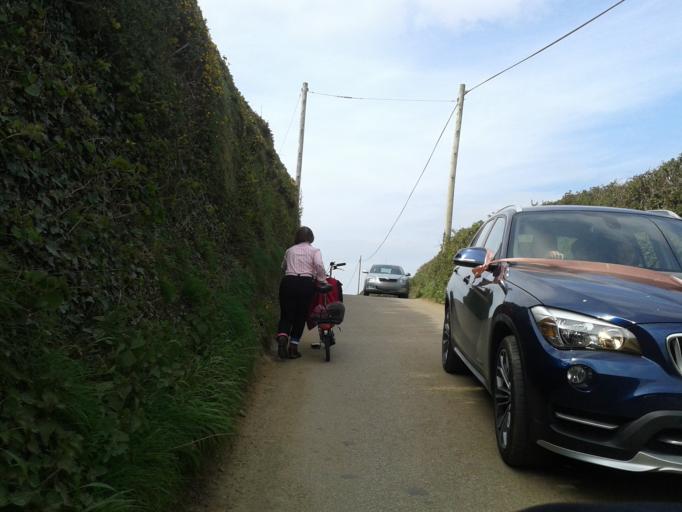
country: GB
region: England
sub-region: Devon
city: Braunton
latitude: 51.1201
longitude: -4.1762
